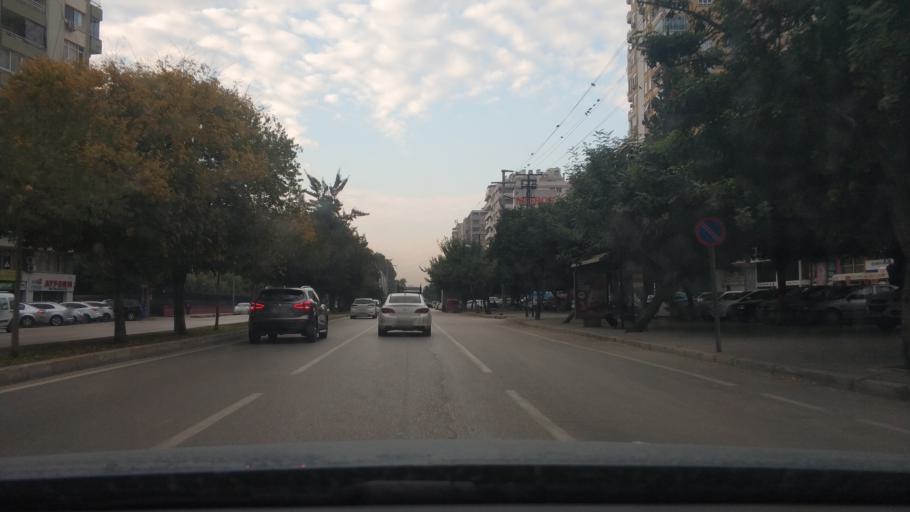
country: TR
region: Adana
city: Adana
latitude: 36.9987
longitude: 35.3173
